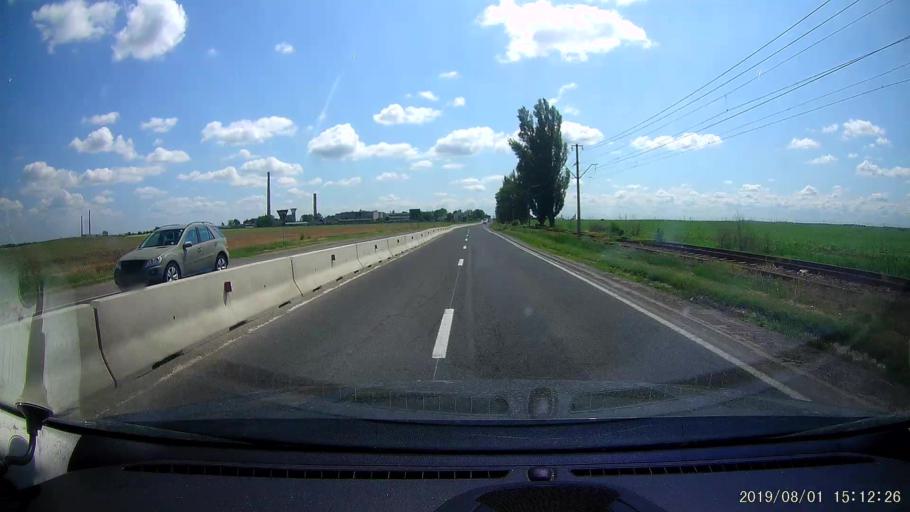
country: RO
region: Braila
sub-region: Comuna Chiscani
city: Lacu Sarat
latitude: 45.2070
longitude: 27.9144
